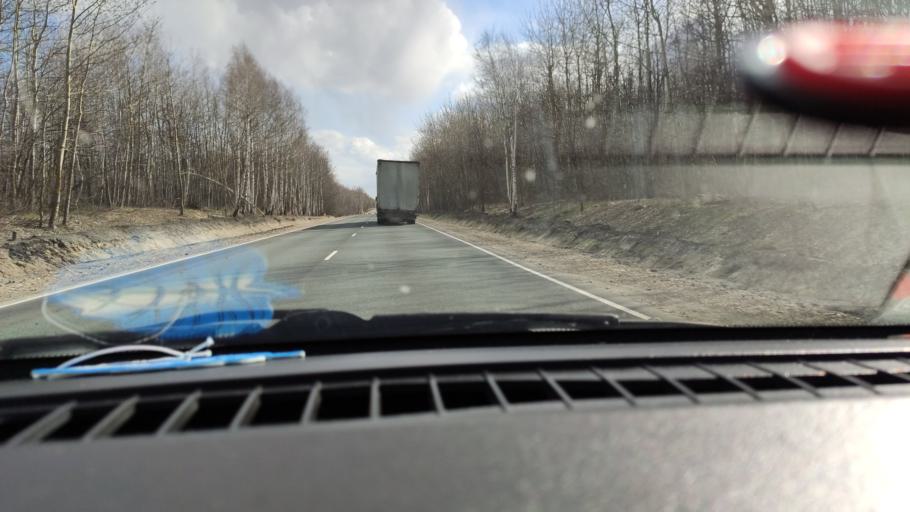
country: RU
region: Saratov
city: Khvalynsk
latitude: 52.4302
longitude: 48.0088
